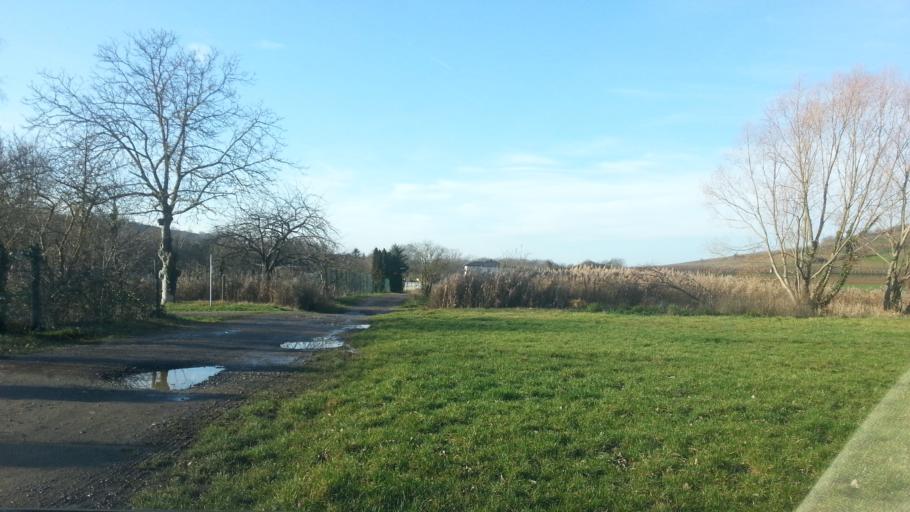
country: DE
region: Rheinland-Pfalz
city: Molsheim
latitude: 49.6401
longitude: 8.1697
